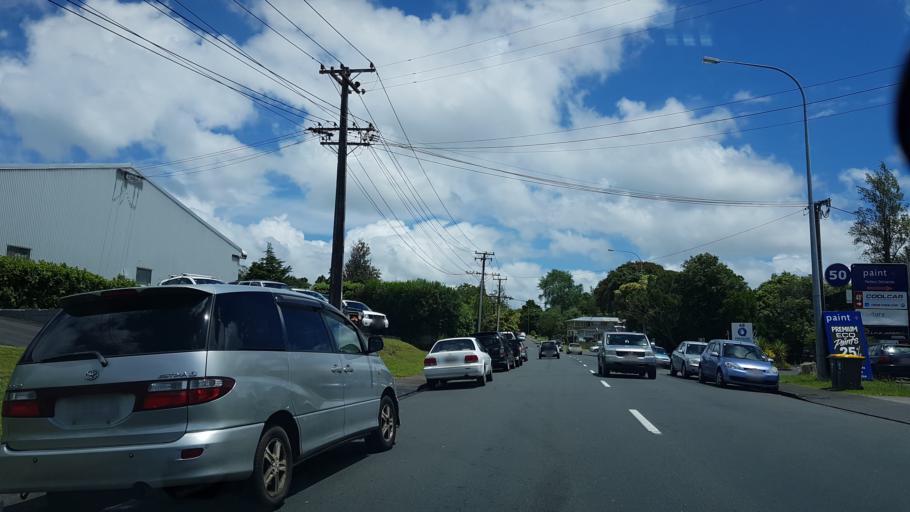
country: NZ
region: Auckland
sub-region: Auckland
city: North Shore
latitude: -36.7755
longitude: 174.7328
